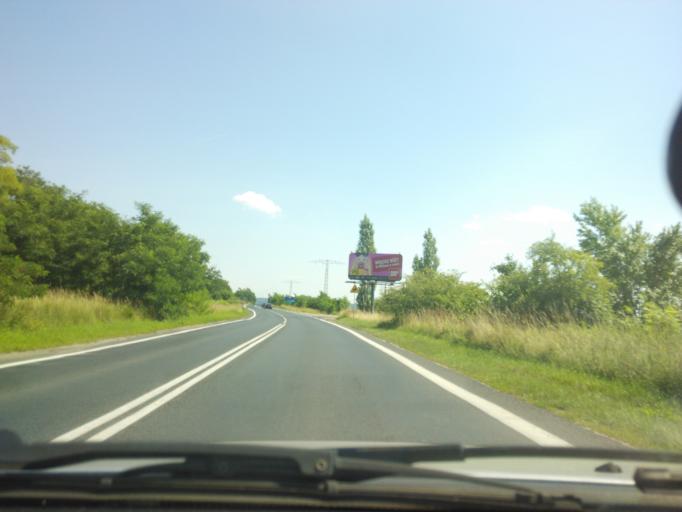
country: PL
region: West Pomeranian Voivodeship
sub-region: Szczecin
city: Szczecin
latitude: 53.3850
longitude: 14.5293
